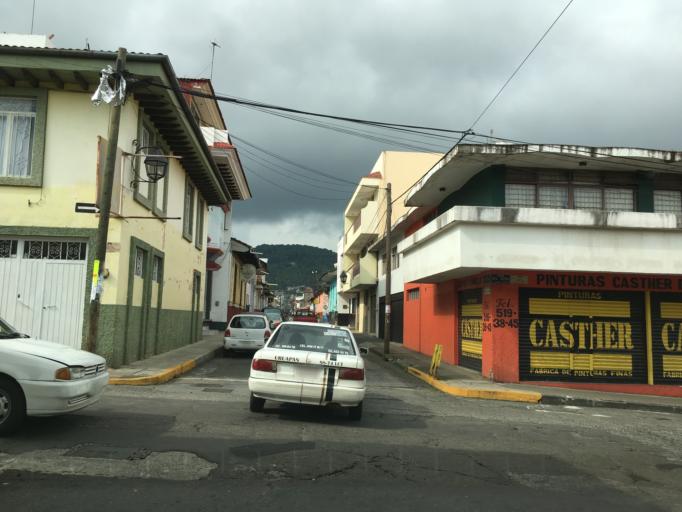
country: MX
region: Michoacan
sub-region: Uruapan
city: Uruapan
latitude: 19.4222
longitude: -102.0682
